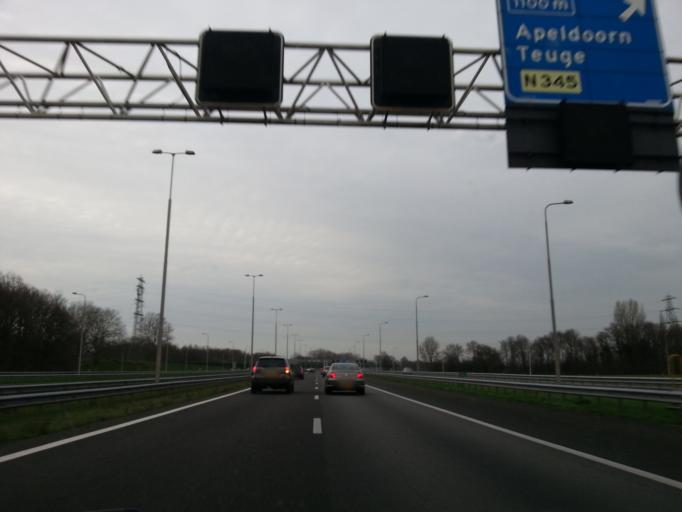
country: NL
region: Gelderland
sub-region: Gemeente Apeldoorn
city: Apeldoorn
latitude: 52.1890
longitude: 6.0223
